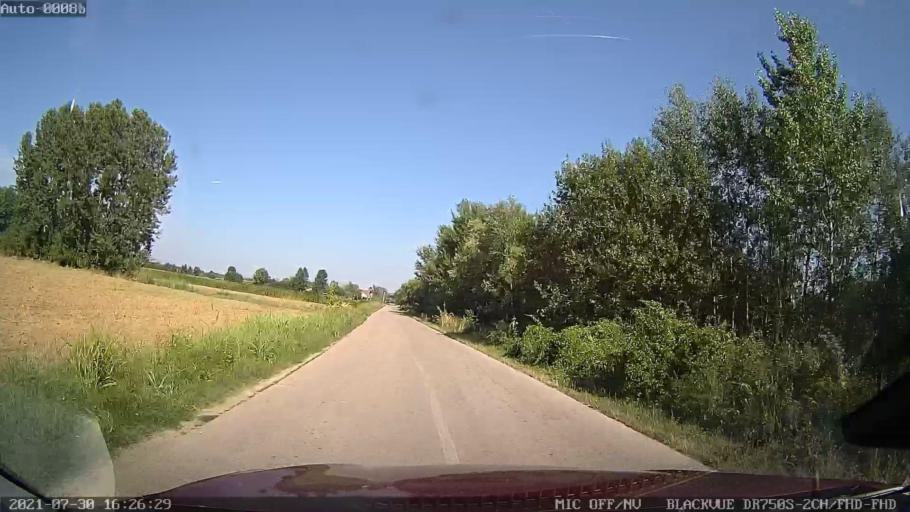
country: HR
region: Varazdinska
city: Jalzabet
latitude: 46.2777
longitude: 16.4237
